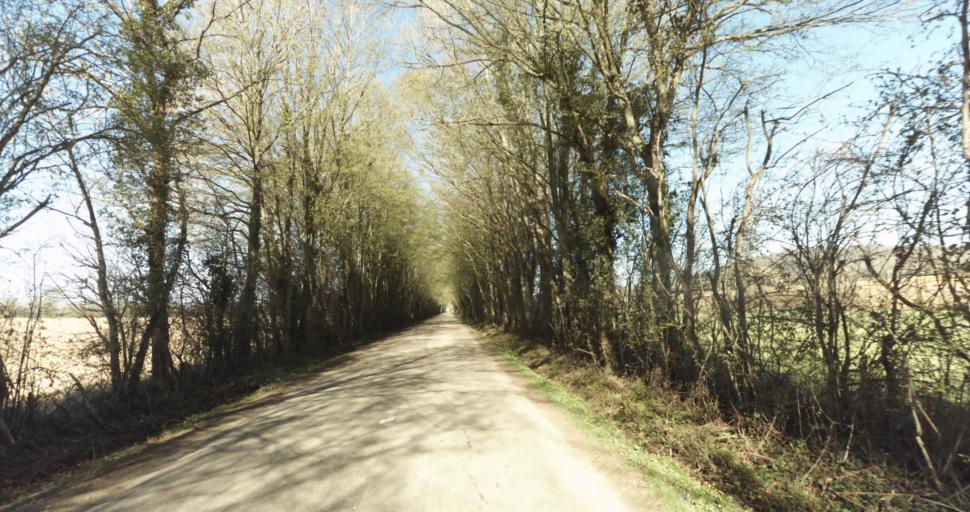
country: FR
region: Lower Normandy
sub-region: Departement du Calvados
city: Livarot
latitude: 48.9671
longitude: 0.0557
